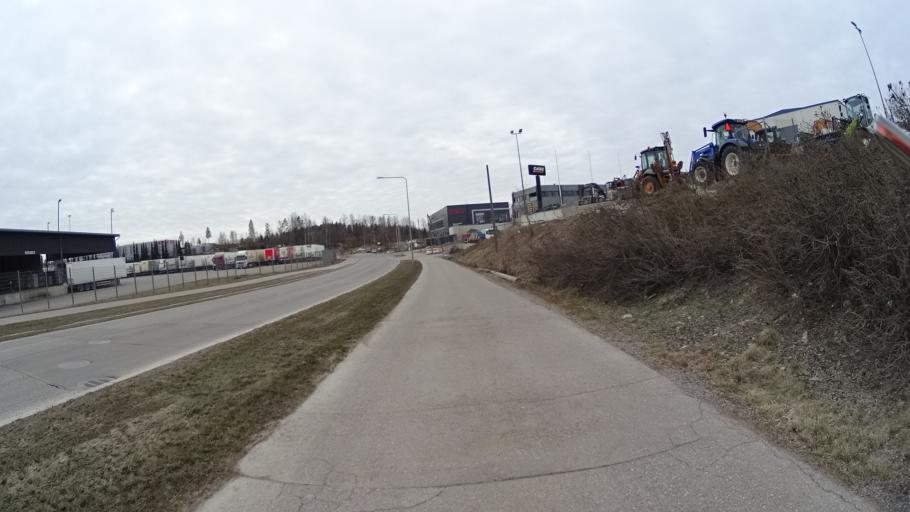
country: FI
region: Uusimaa
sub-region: Helsinki
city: Teekkarikylae
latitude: 60.3007
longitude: 24.9051
